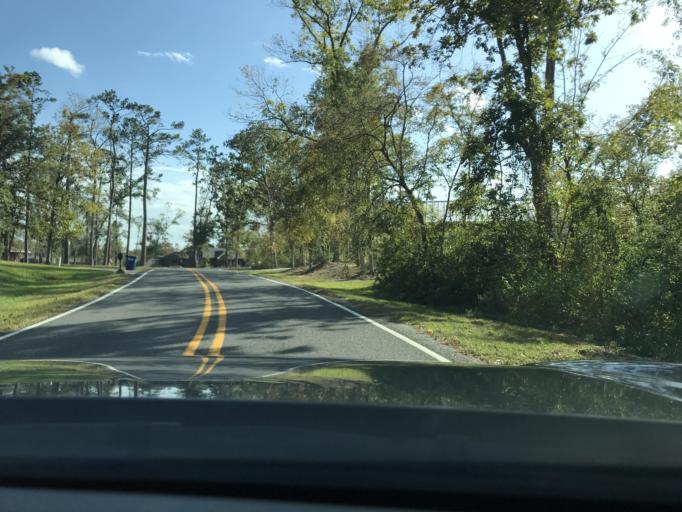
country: US
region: Louisiana
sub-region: Calcasieu Parish
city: Westlake
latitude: 30.3207
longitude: -93.2901
